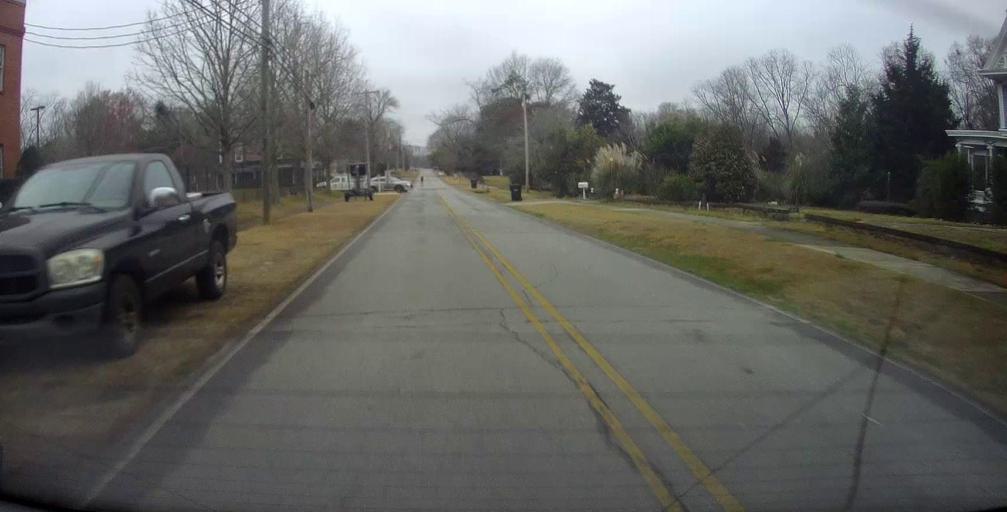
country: US
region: Georgia
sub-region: Lamar County
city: Barnesville
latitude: 33.0546
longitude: -84.1593
